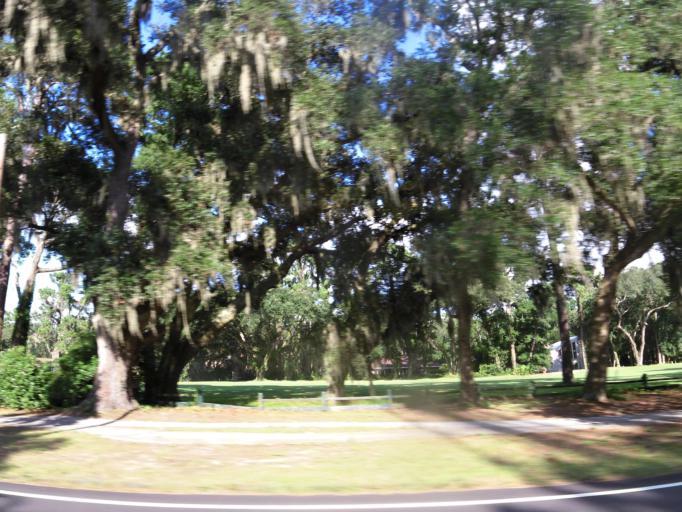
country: US
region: Georgia
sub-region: Glynn County
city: Saint Simon Mills
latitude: 31.1913
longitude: -81.3766
